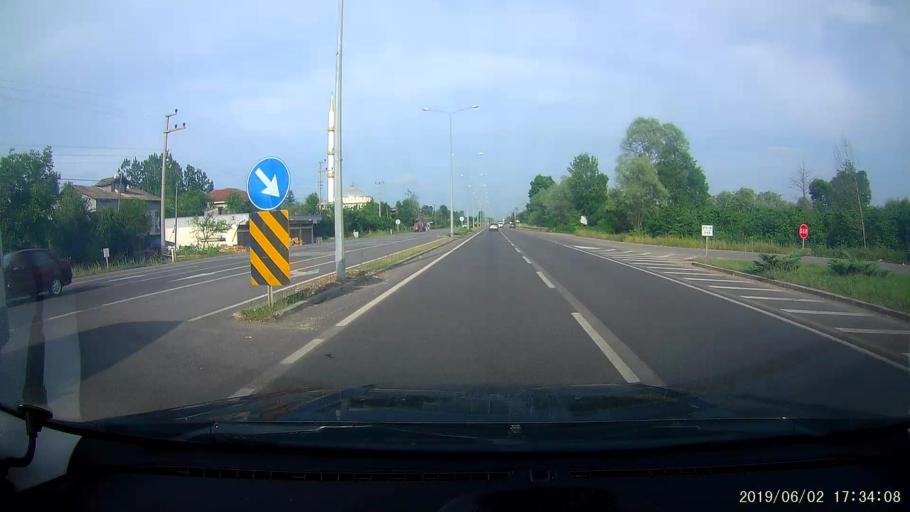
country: TR
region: Samsun
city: Terme
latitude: 41.2205
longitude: 36.8627
